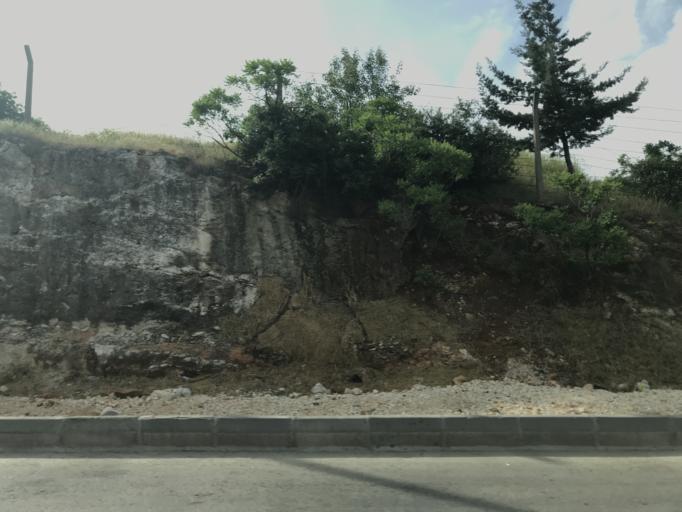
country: TR
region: Gaziantep
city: Sehitkamil
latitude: 37.1583
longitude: 37.2866
